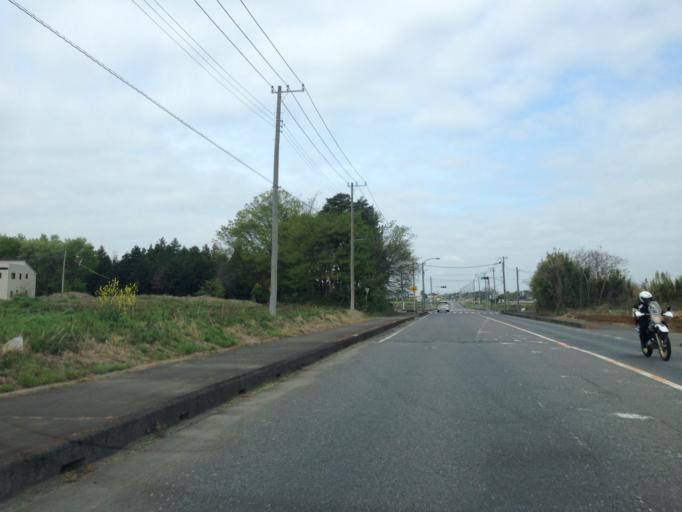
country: JP
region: Ibaraki
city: Ishige
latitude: 36.1473
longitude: 140.0250
